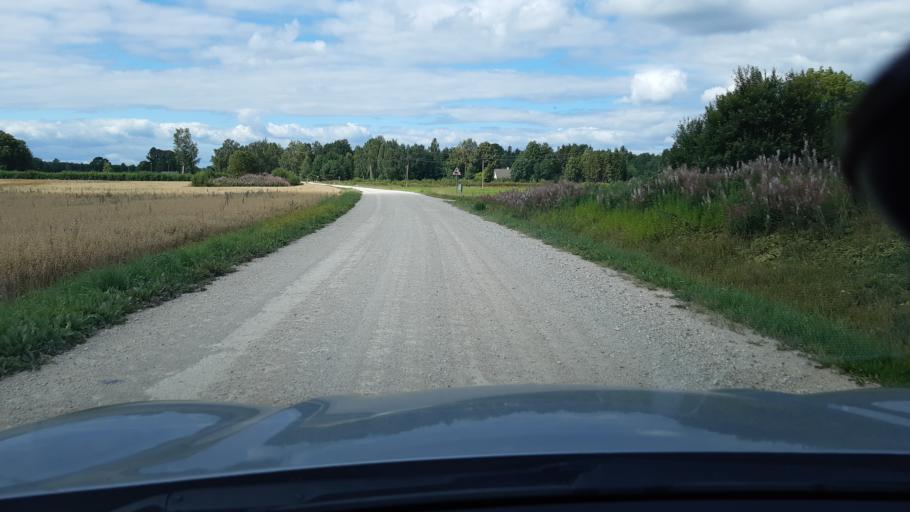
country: EE
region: Paernumaa
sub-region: Vaendra vald (alev)
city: Vandra
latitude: 58.7939
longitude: 25.0039
